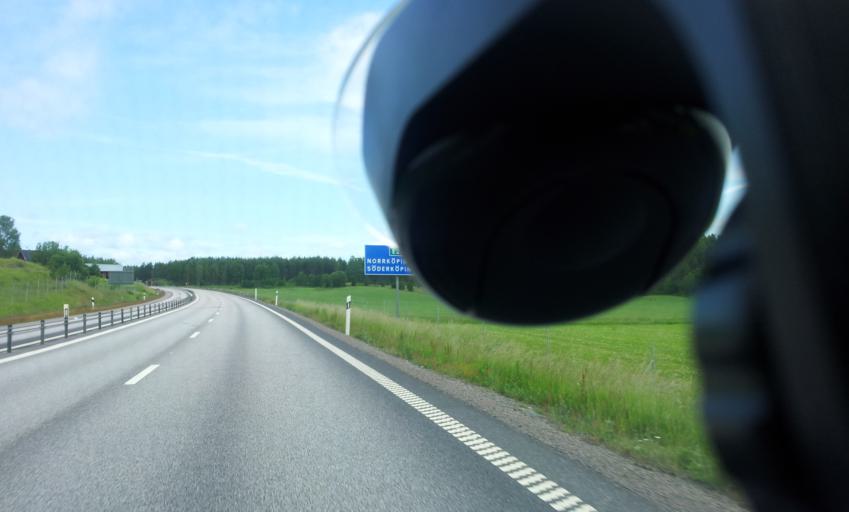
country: SE
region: OEstergoetland
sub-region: Valdemarsviks Kommun
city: Valdemarsvik
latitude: 58.2266
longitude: 16.5527
